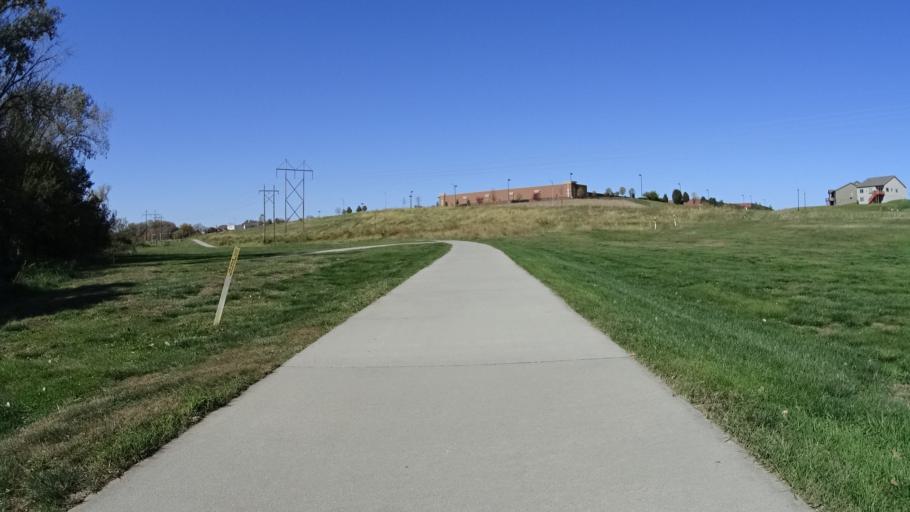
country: US
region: Nebraska
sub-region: Sarpy County
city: La Vista
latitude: 41.1683
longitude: -96.0184
